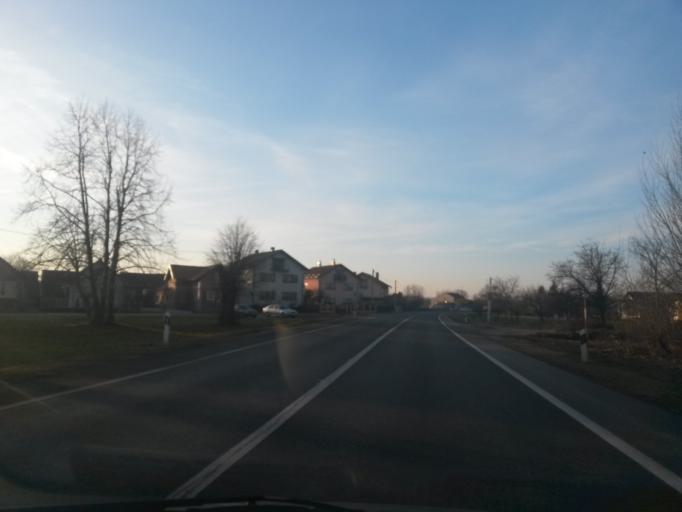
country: HR
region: Varazdinska
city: Jalzabet
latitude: 46.2985
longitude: 16.4848
